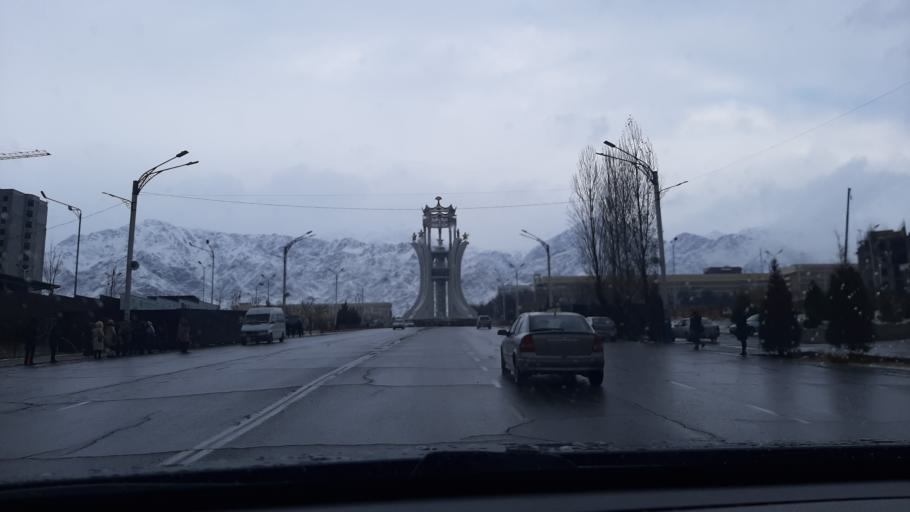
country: TJ
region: Viloyati Sughd
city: Khujand
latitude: 40.2996
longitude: 69.6147
